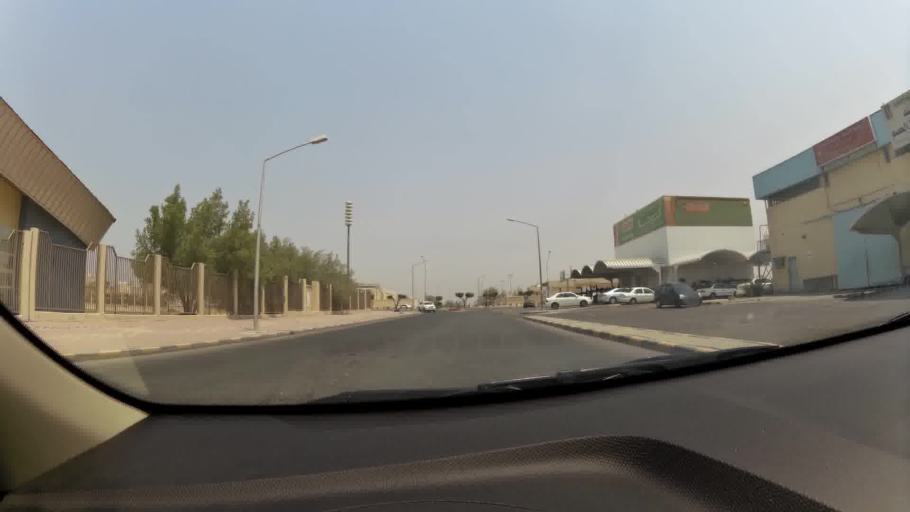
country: KW
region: Al Asimah
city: Ar Rabiyah
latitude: 29.3124
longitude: 47.8180
